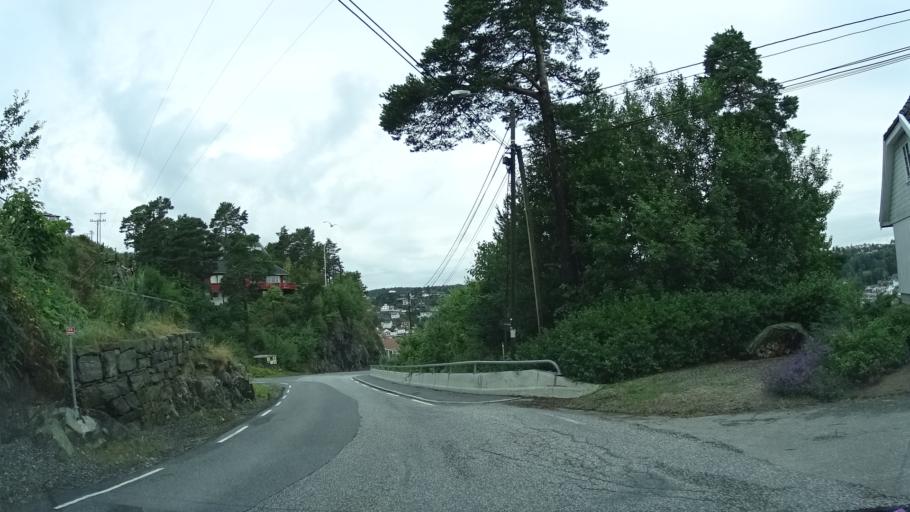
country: NO
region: Aust-Agder
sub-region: Arendal
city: Arendal
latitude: 58.4516
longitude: 8.7620
